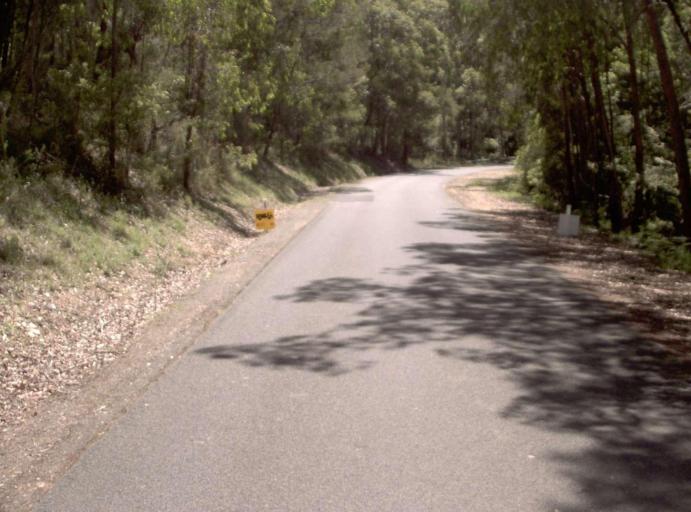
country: AU
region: New South Wales
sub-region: Bombala
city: Bombala
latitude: -37.5156
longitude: 148.9288
